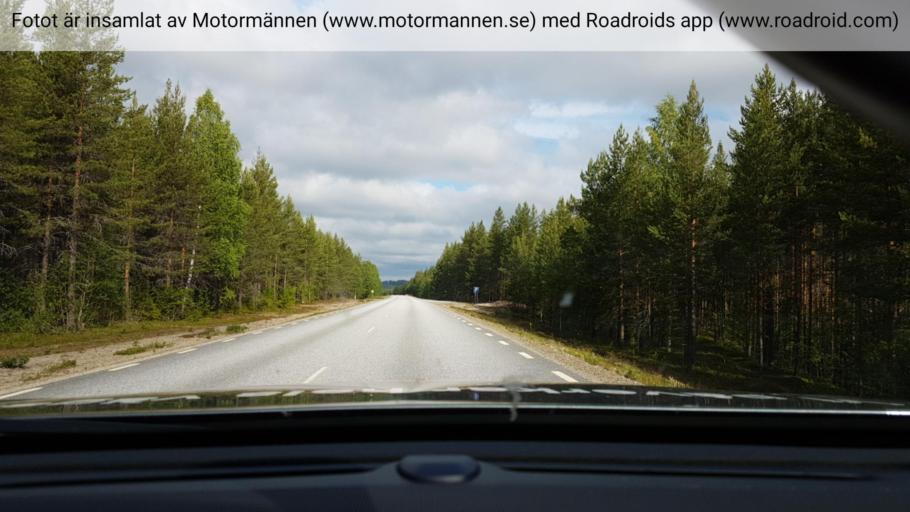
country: SE
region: Vaesterbotten
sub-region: Vindelns Kommun
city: Vindeln
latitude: 64.3774
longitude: 19.4013
